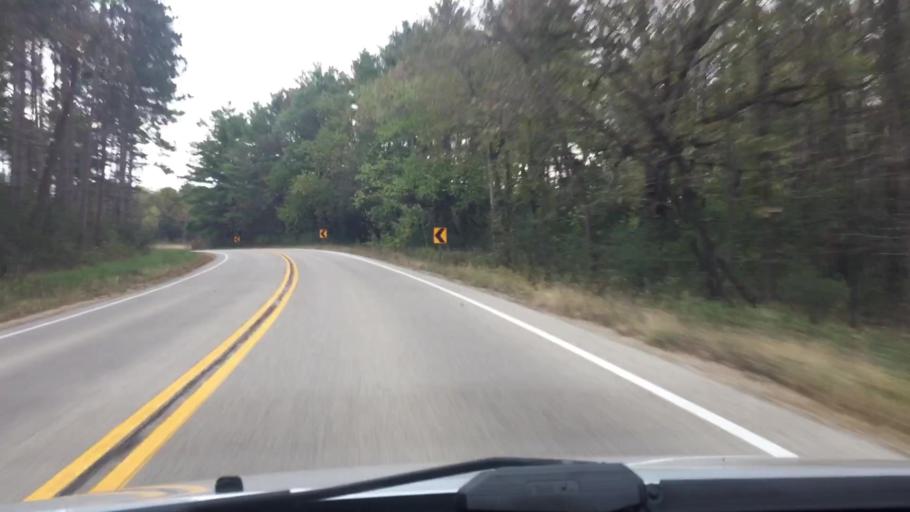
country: US
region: Wisconsin
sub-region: Waukesha County
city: Eagle
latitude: 42.9180
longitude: -88.4734
